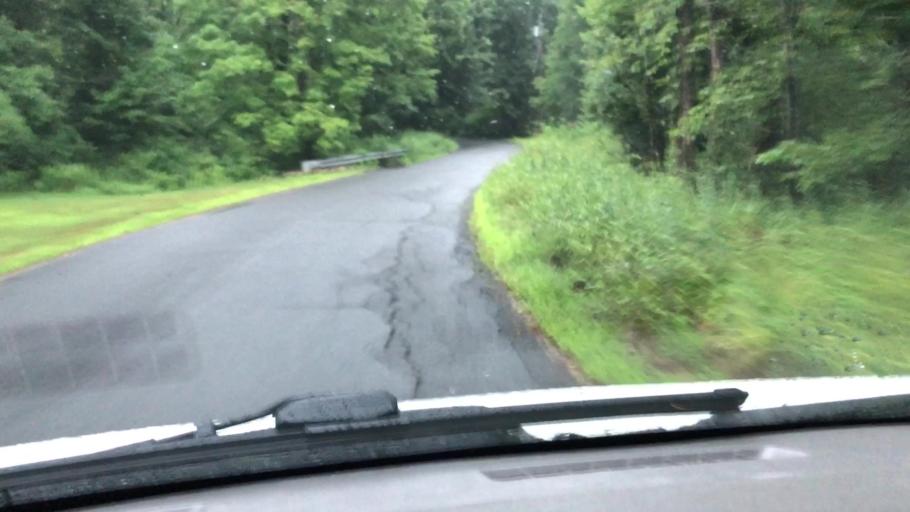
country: US
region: Massachusetts
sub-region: Hampshire County
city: Southampton
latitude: 42.2436
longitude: -72.7059
